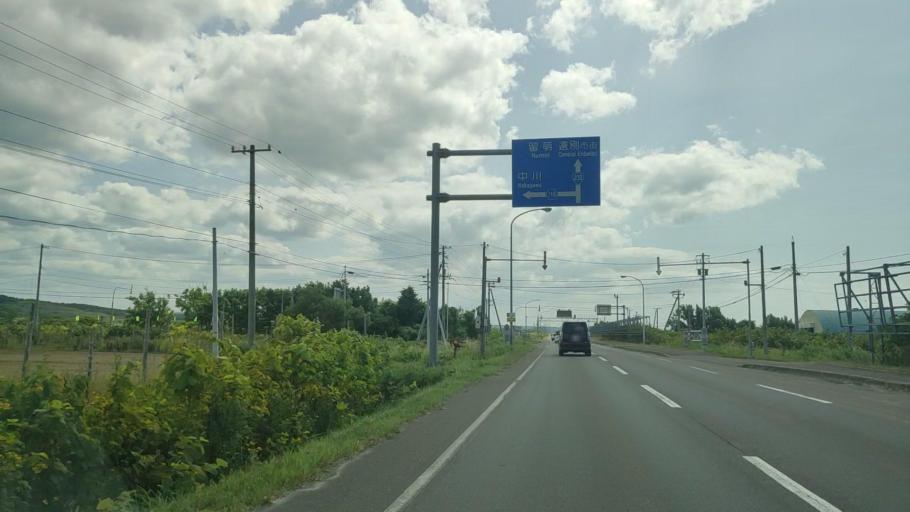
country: JP
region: Hokkaido
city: Makubetsu
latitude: 44.7562
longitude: 141.7946
